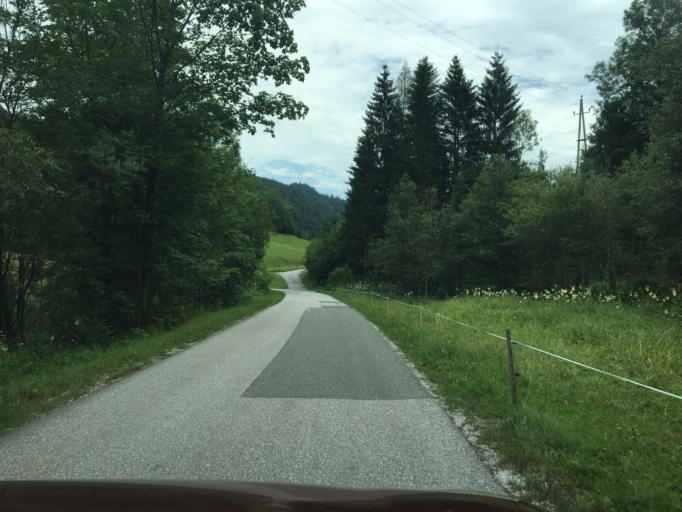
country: AT
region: Salzburg
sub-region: Politischer Bezirk Hallein
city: Scheffau am Tennengebirge
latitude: 47.6195
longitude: 13.2477
